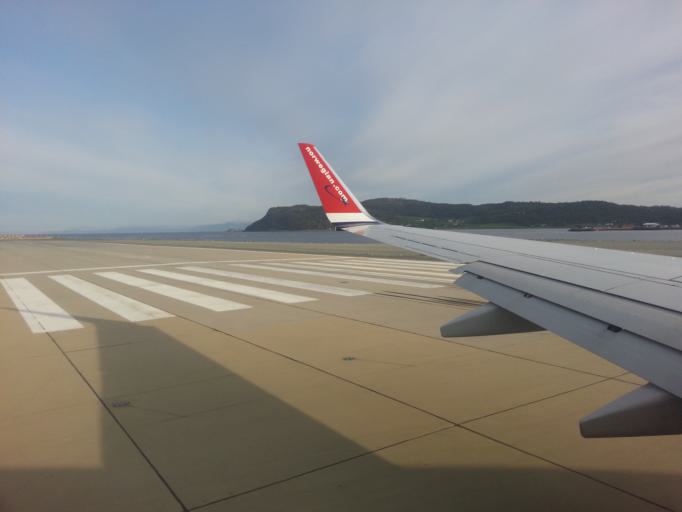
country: NO
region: Nord-Trondelag
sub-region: Stjordal
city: Stjordal
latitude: 63.4574
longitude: 10.8922
